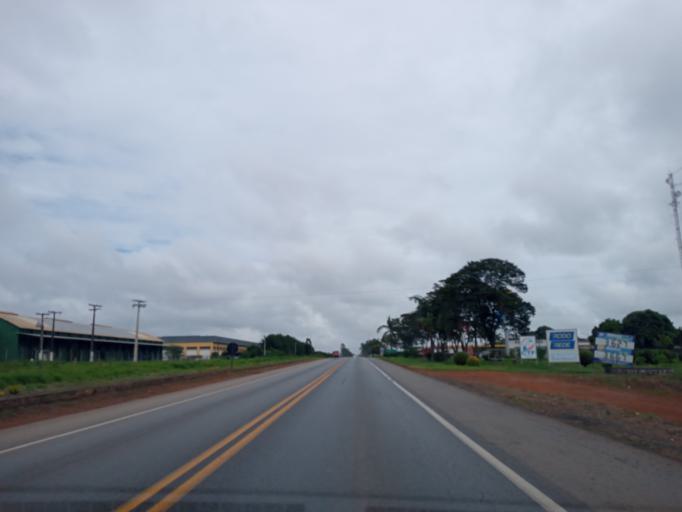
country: BR
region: Minas Gerais
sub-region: Campos Altos
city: Campos Altos
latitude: -19.6587
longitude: -46.2103
